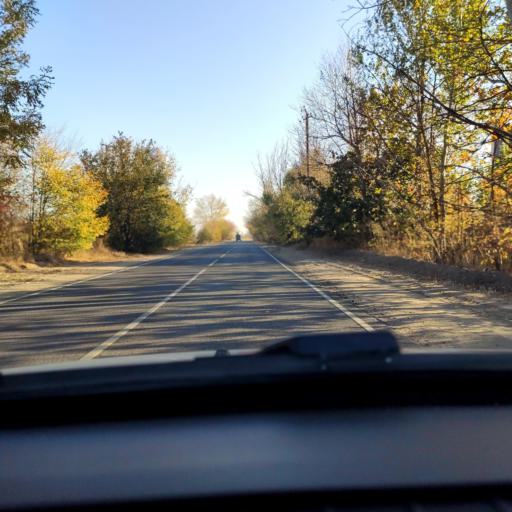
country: RU
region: Voronezj
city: Shilovo
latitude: 51.5685
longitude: 39.1390
